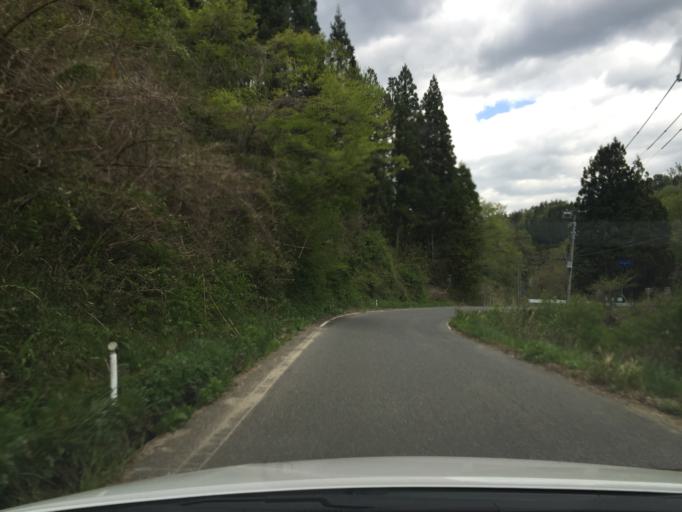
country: JP
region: Fukushima
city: Hobaramachi
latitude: 37.7206
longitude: 140.6429
